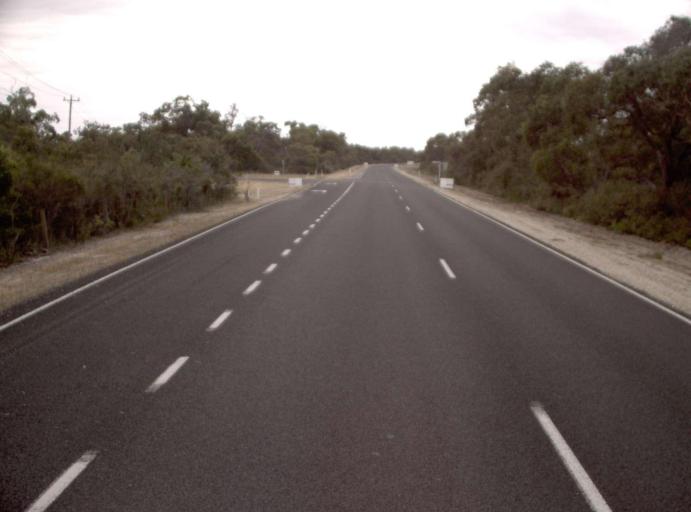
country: AU
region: Victoria
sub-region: East Gippsland
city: Bairnsdale
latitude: -38.1263
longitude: 147.4317
